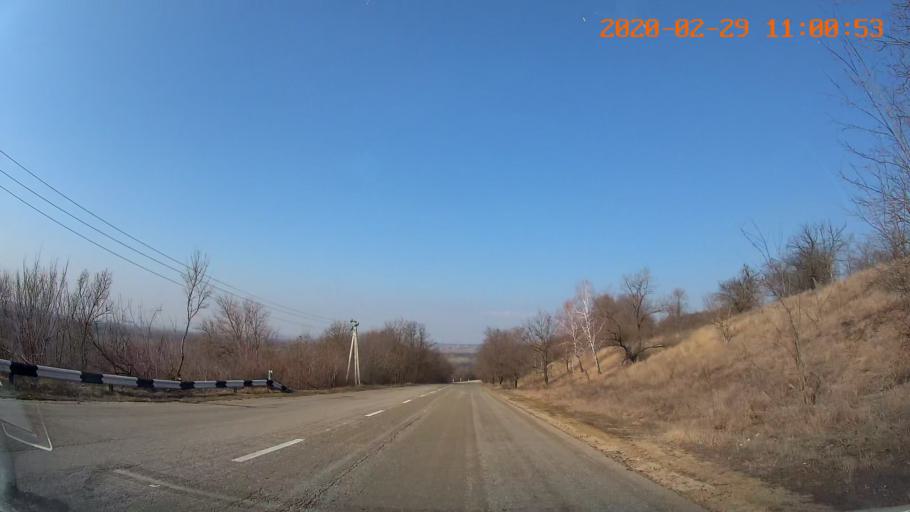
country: MD
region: Telenesti
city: Grigoriopol
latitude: 47.1609
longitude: 29.2688
